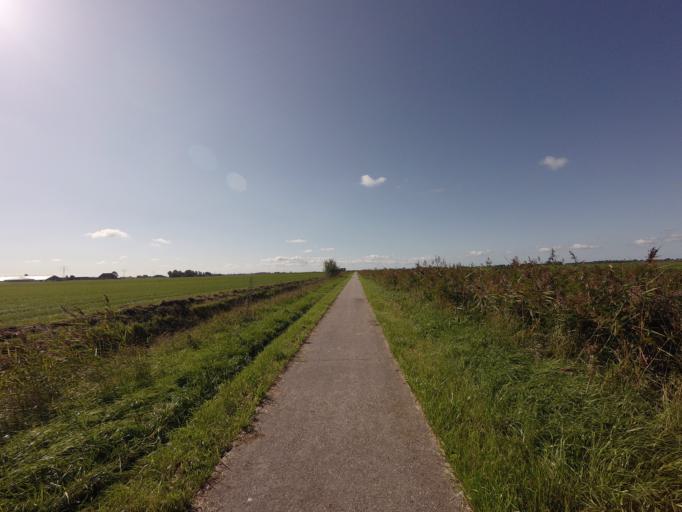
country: NL
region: Friesland
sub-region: Gemeente Boarnsterhim
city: Reduzum
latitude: 53.1395
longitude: 5.7622
